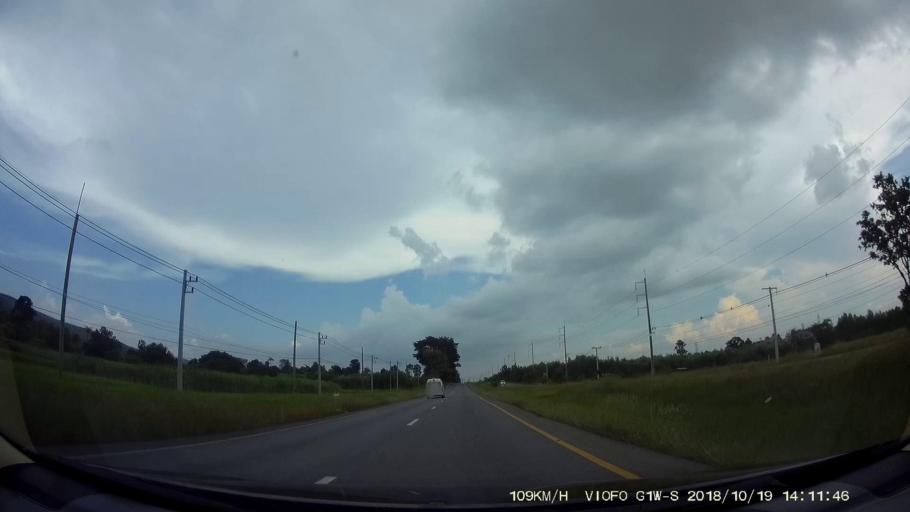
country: TH
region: Chaiyaphum
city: Khon Sawan
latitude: 15.9419
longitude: 102.1650
